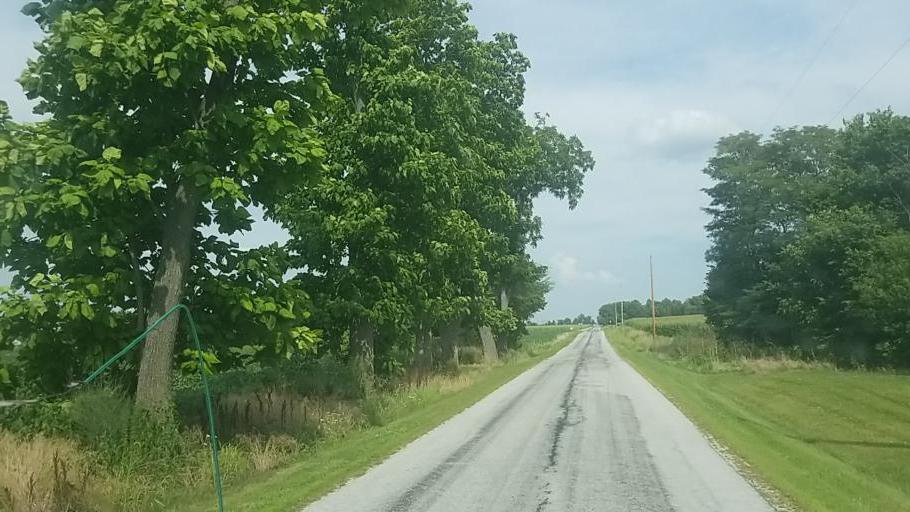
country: US
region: Ohio
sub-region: Hardin County
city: Forest
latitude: 40.8176
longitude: -83.4508
